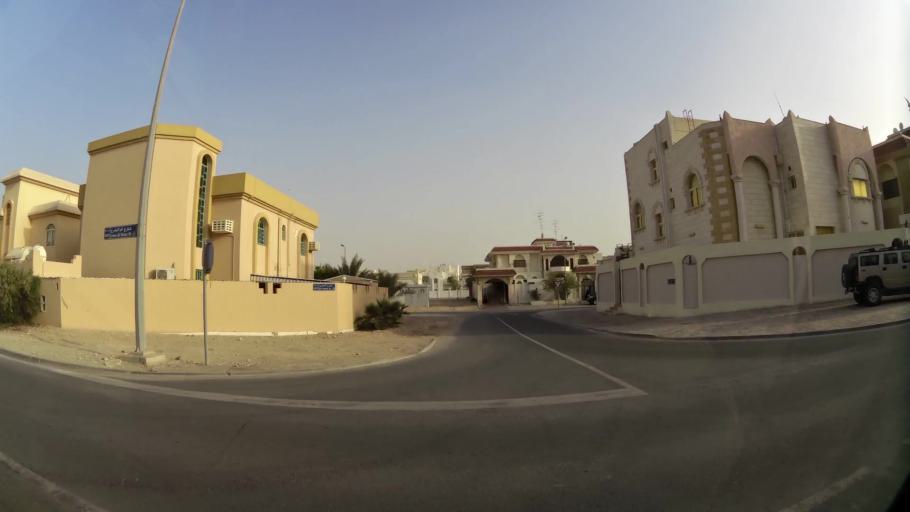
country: QA
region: Baladiyat ar Rayyan
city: Ar Rayyan
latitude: 25.2525
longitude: 51.4429
